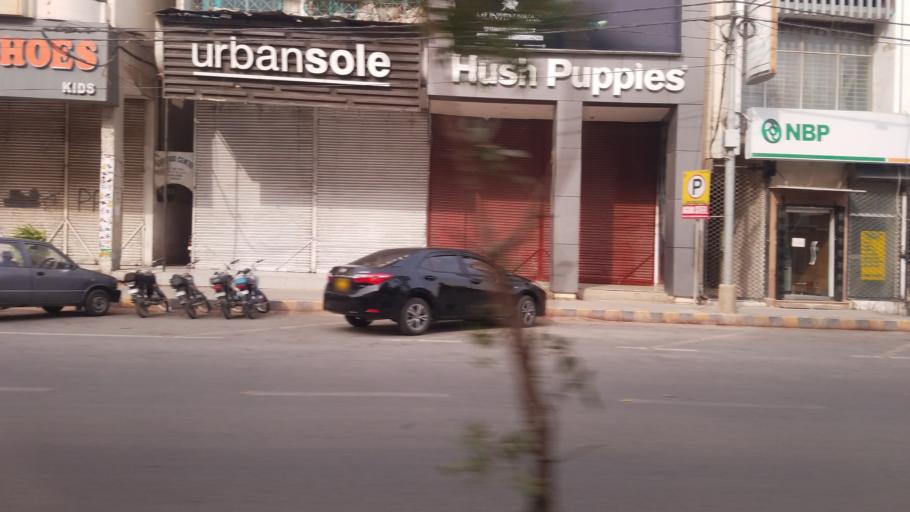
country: PK
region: Sindh
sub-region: Karachi District
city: Karachi
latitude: 24.8689
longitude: 67.0580
